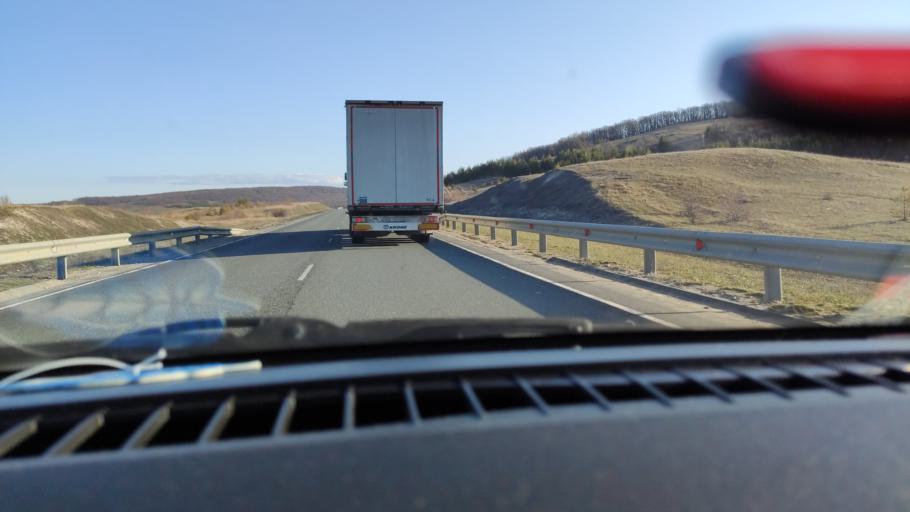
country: RU
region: Saratov
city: Alekseyevka
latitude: 52.3827
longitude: 47.9736
